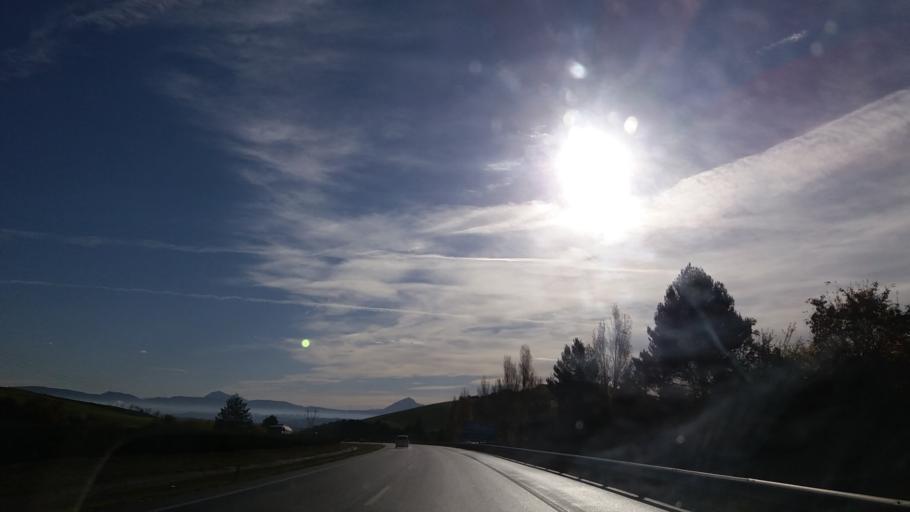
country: ES
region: Navarre
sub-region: Provincia de Navarra
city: Oltza
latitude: 42.8601
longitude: -1.7438
